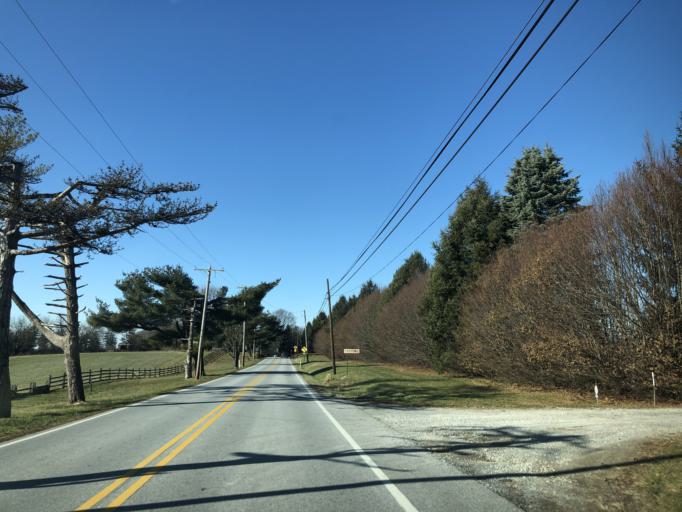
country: US
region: Pennsylvania
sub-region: Chester County
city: Upland
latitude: 39.8999
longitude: -75.7551
